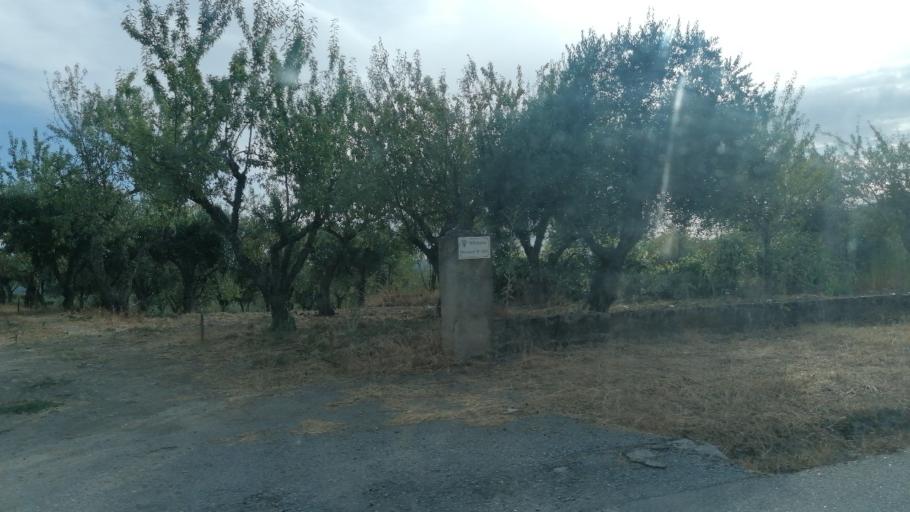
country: PT
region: Viseu
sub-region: Sao Joao da Pesqueira
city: Sao Joao da Pesqueira
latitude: 41.0990
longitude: -7.3809
